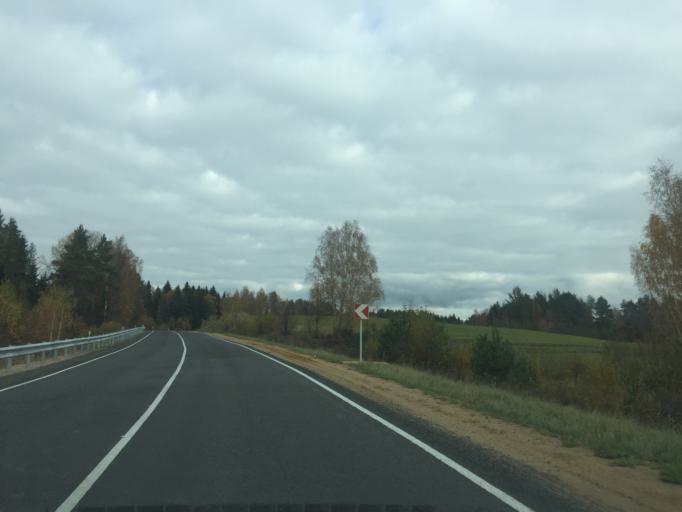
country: BY
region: Minsk
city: Svir
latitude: 54.8638
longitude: 26.3386
